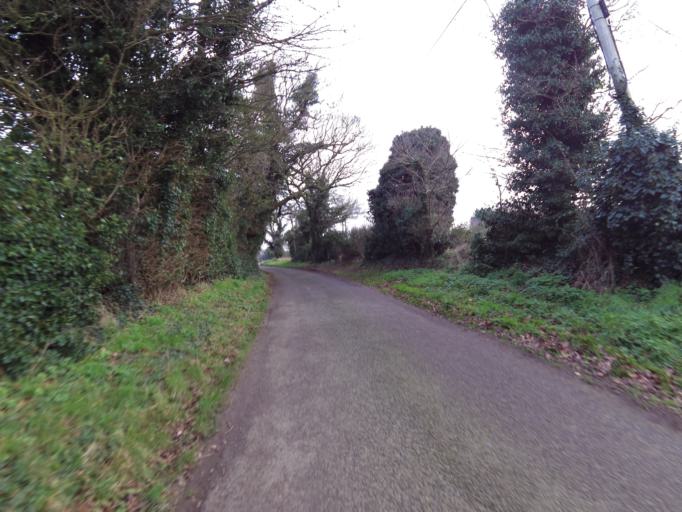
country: GB
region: England
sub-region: Suffolk
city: Woodbridge
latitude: 52.0607
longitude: 1.3138
